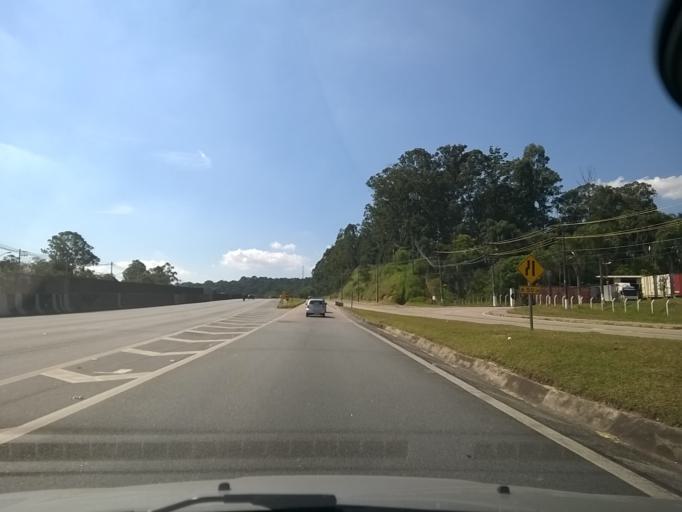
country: BR
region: Sao Paulo
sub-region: Caieiras
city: Caieiras
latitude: -23.4280
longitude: -46.7872
